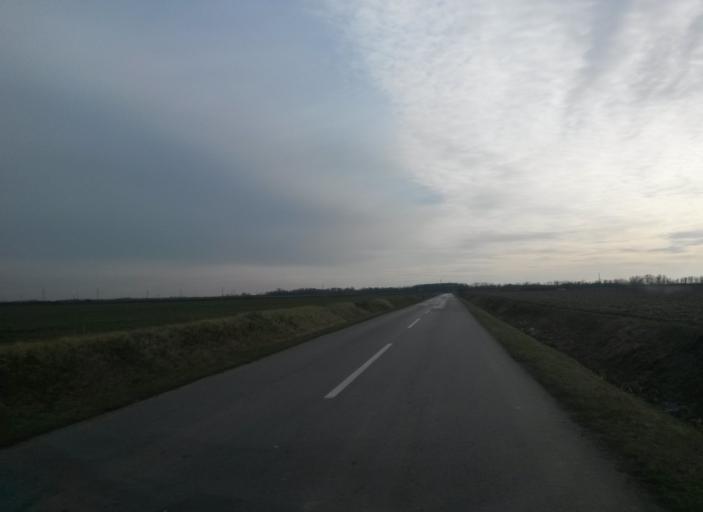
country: HR
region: Osjecko-Baranjska
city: Ovcara
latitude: 45.5073
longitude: 18.5959
